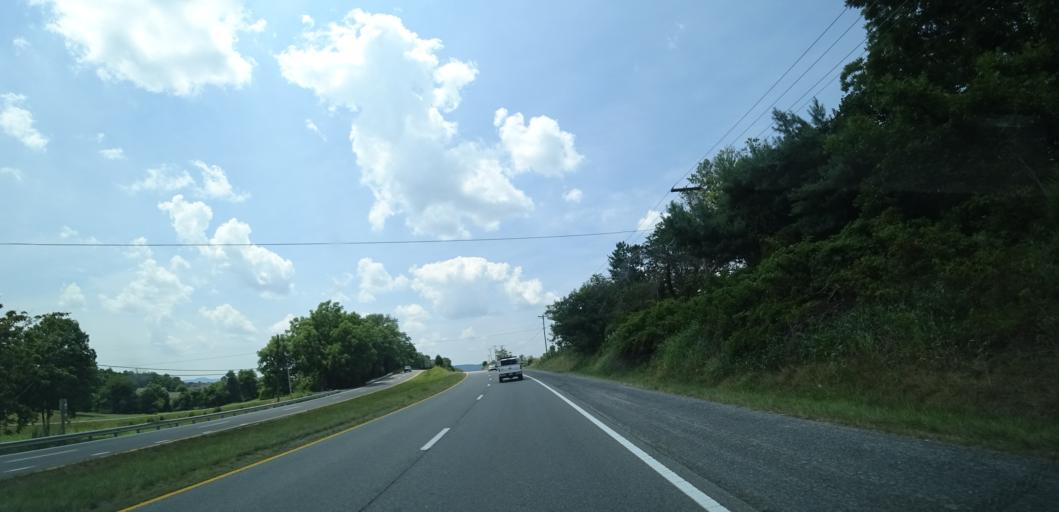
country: US
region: Virginia
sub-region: Botetourt County
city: Daleville
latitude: 37.4516
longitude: -79.8983
